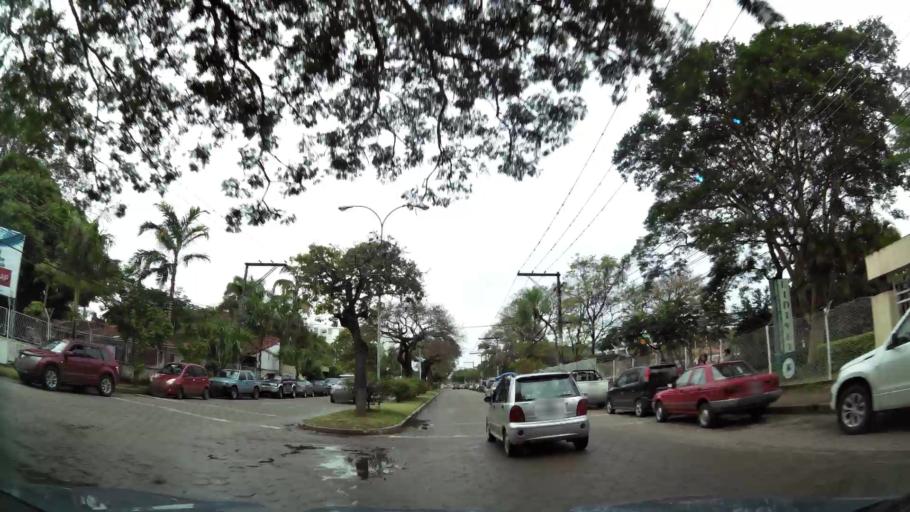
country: BO
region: Santa Cruz
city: Santa Cruz de la Sierra
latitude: -17.7940
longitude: -63.1825
